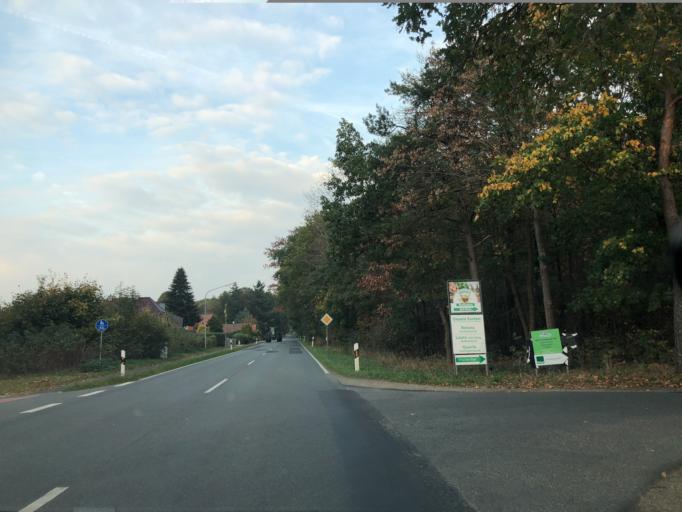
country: DE
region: Lower Saxony
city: Papenburg
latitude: 53.0567
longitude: 7.4076
